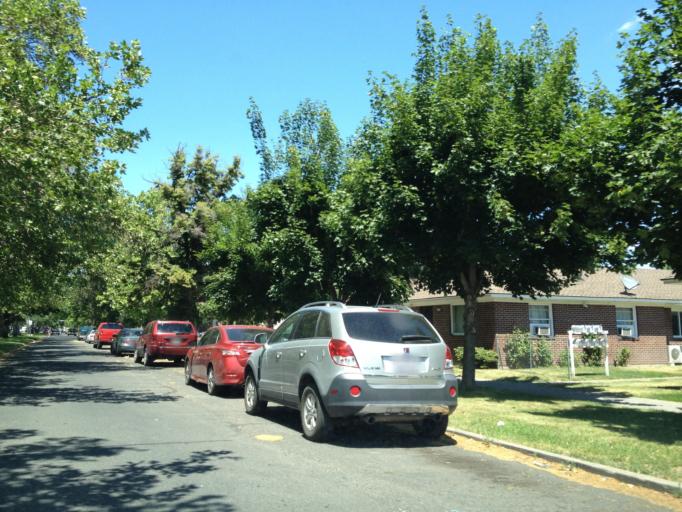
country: US
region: Washington
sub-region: Yakima County
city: Yakima
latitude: 46.6011
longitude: -120.4988
